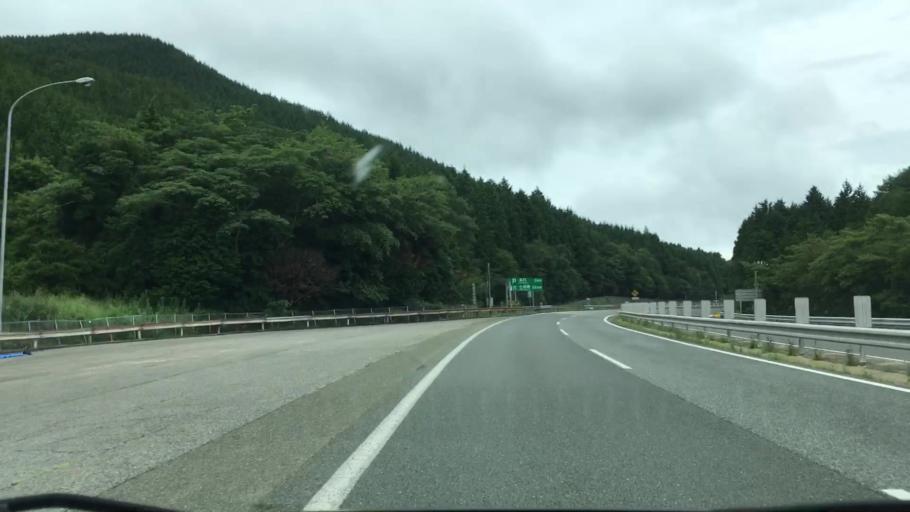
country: JP
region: Hiroshima
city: Shobara
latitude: 34.8715
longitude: 133.1468
